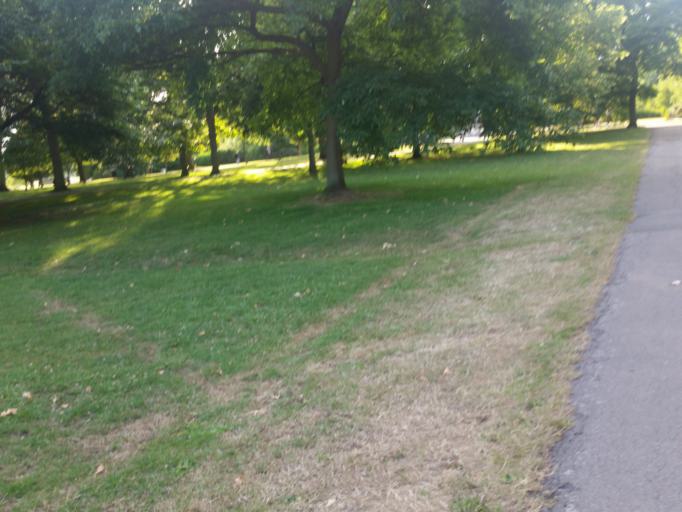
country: GB
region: England
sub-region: Greater London
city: Camden Town
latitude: 51.5324
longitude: -0.1493
